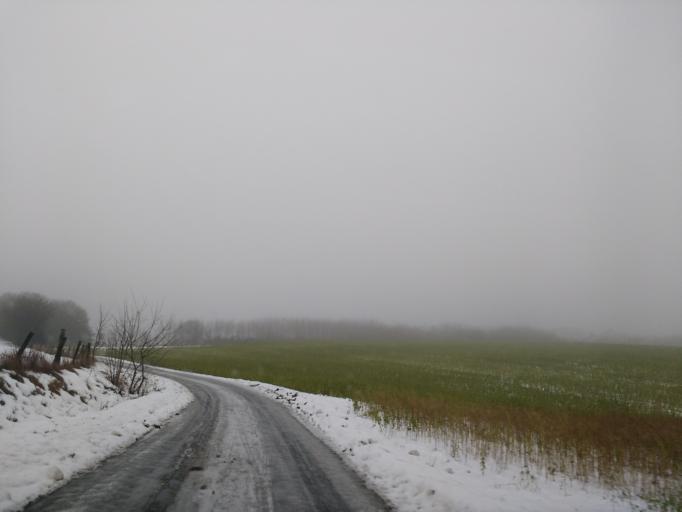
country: DE
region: North Rhine-Westphalia
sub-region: Regierungsbezirk Detmold
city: Altenbeken
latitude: 51.8068
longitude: 8.9375
